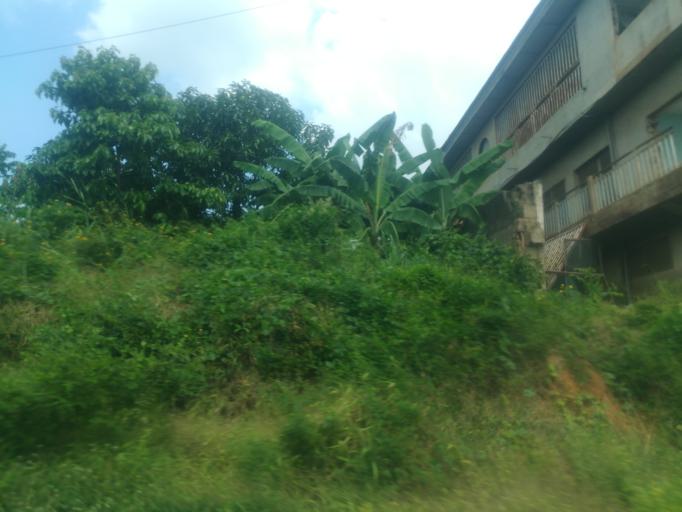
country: NG
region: Oyo
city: Ibadan
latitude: 7.4225
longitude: 3.8437
